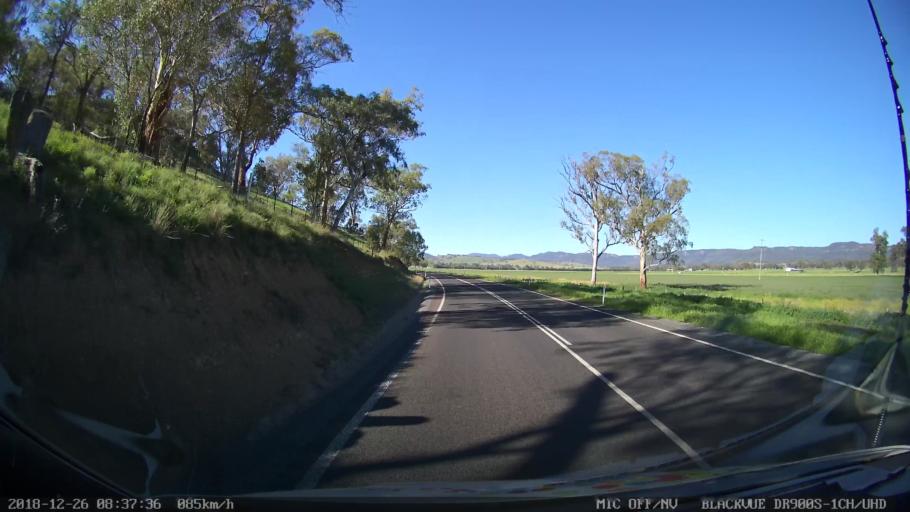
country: AU
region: New South Wales
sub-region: Upper Hunter Shire
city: Merriwa
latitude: -32.4337
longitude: 150.0884
